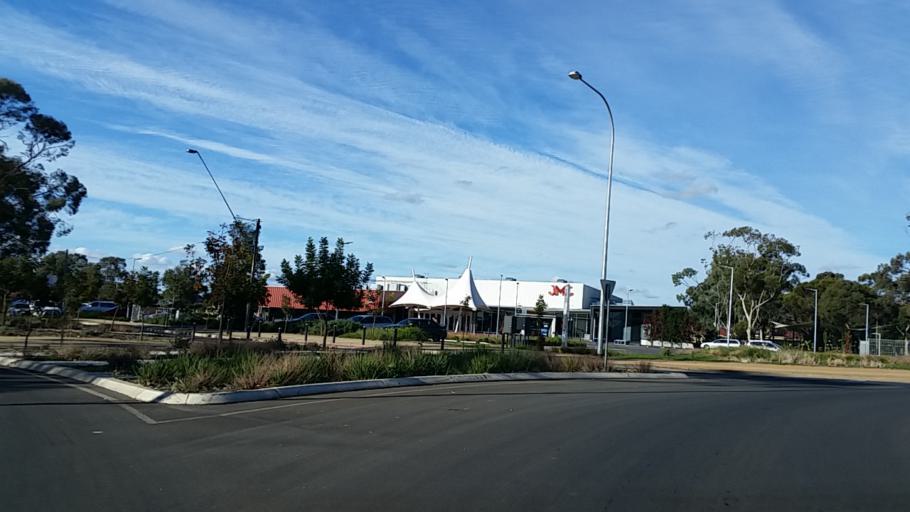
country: AU
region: South Australia
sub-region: Playford
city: Smithfield
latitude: -34.6809
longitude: 138.6731
